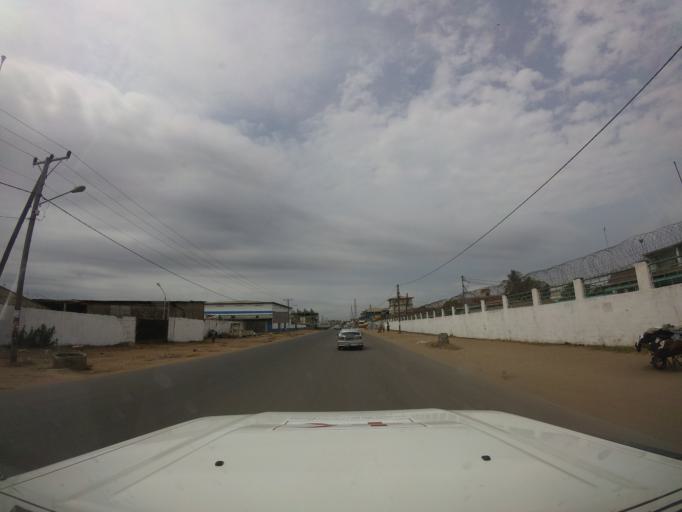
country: LR
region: Montserrado
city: Monrovia
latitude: 6.3557
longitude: -10.7865
